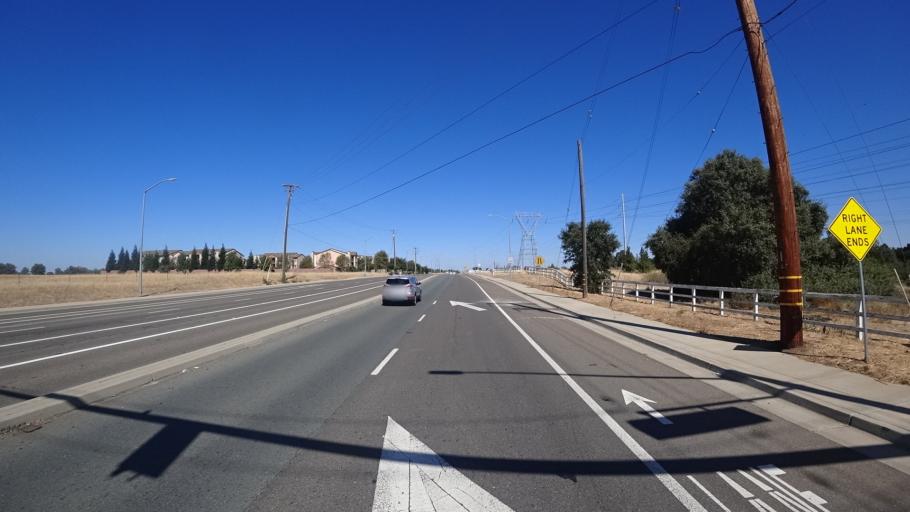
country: US
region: California
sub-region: Sacramento County
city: Elk Grove
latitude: 38.4239
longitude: -121.3531
